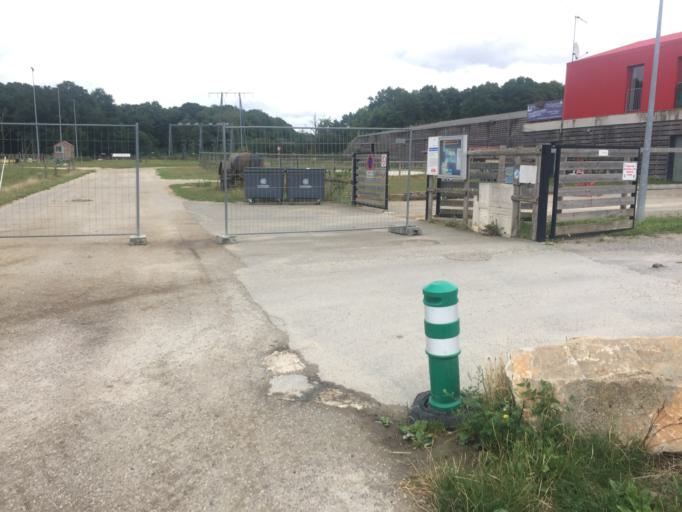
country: FR
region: Ile-de-France
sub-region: Departement des Yvelines
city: Bois-d'Arcy
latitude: 48.8081
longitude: 2.0125
